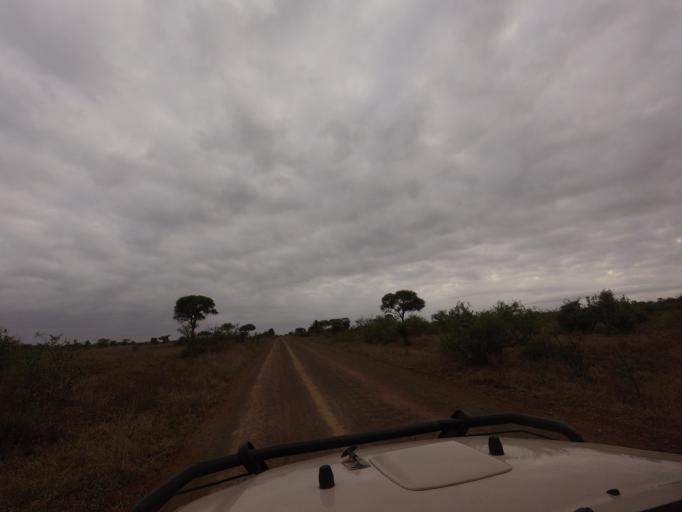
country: ZA
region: Mpumalanga
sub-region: Ehlanzeni District
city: Komatipoort
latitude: -25.3131
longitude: 31.9119
